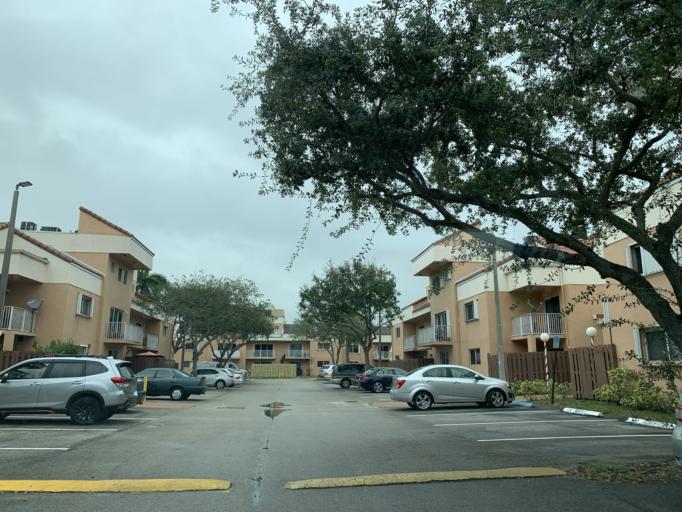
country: US
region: Florida
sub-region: Miami-Dade County
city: Kendall West
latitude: 25.6926
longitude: -80.4353
